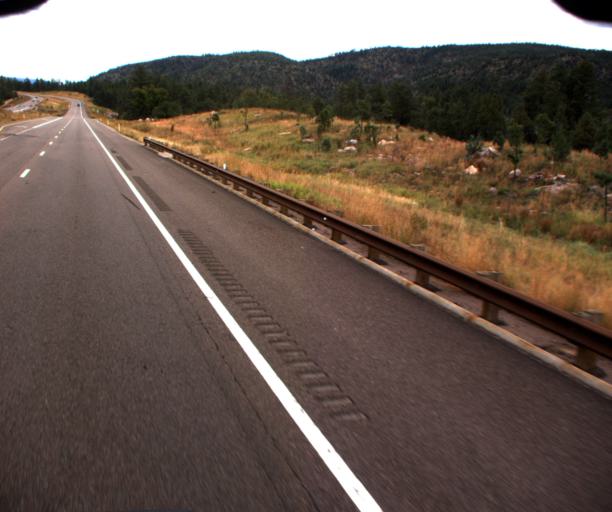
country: US
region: Arizona
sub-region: Gila County
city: Star Valley
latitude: 34.3126
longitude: -111.0526
